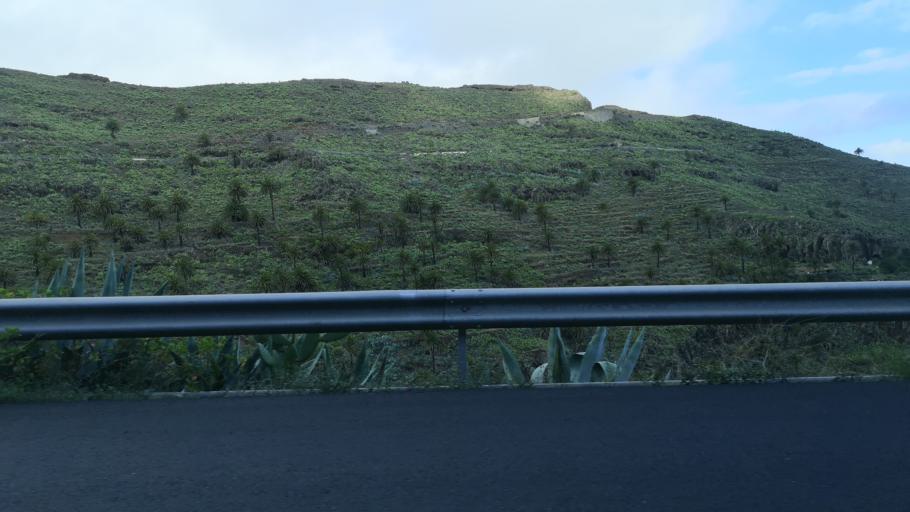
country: ES
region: Canary Islands
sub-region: Provincia de Santa Cruz de Tenerife
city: Alajero
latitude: 28.0737
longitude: -17.2073
